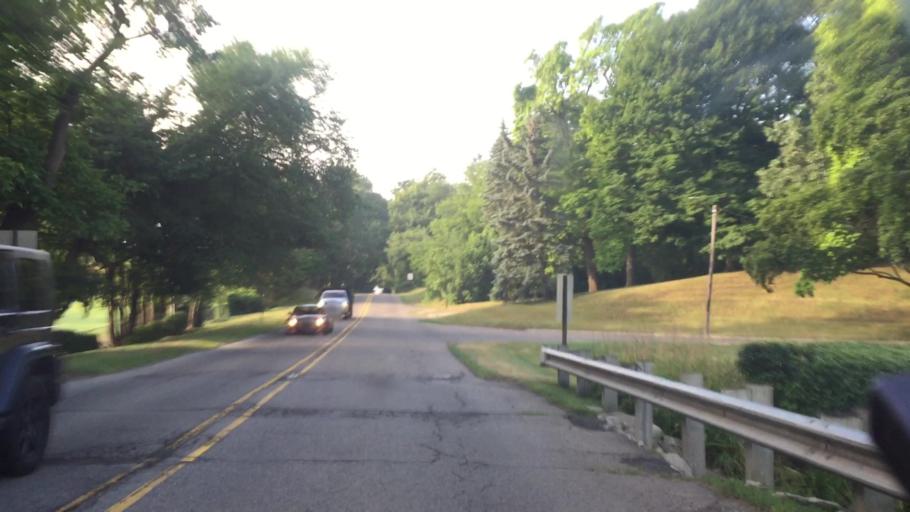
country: US
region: Michigan
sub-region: Oakland County
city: Bloomfield Hills
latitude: 42.5924
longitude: -83.2474
